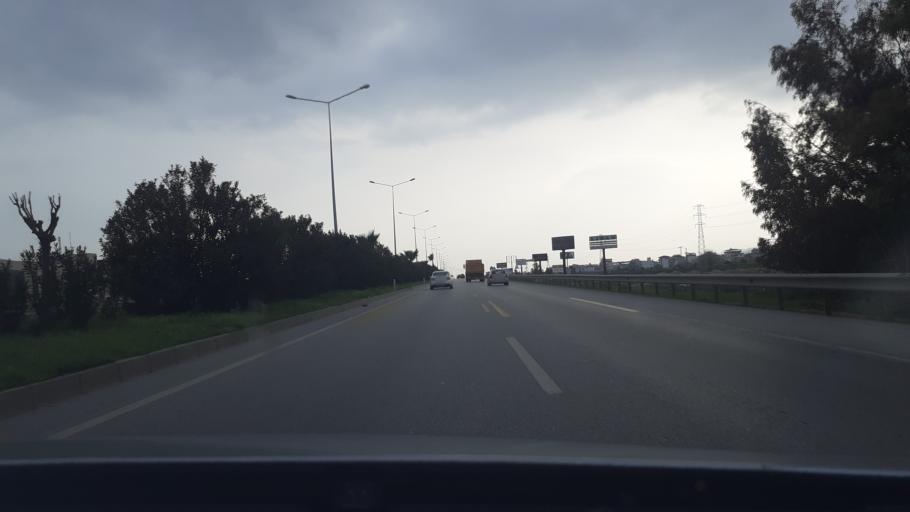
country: TR
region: Hatay
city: Serinyol
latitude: 36.3698
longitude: 36.2249
